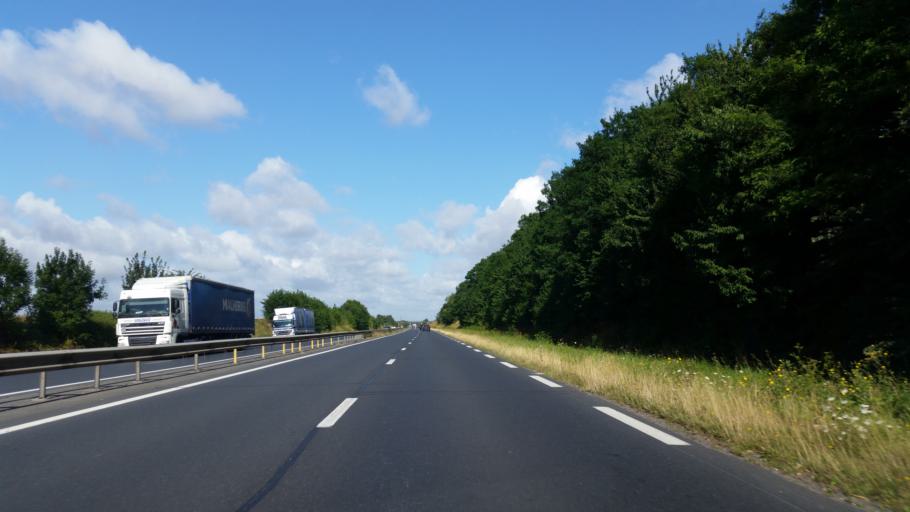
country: FR
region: Lower Normandy
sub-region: Departement du Calvados
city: Rots
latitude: 49.1995
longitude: -0.4825
